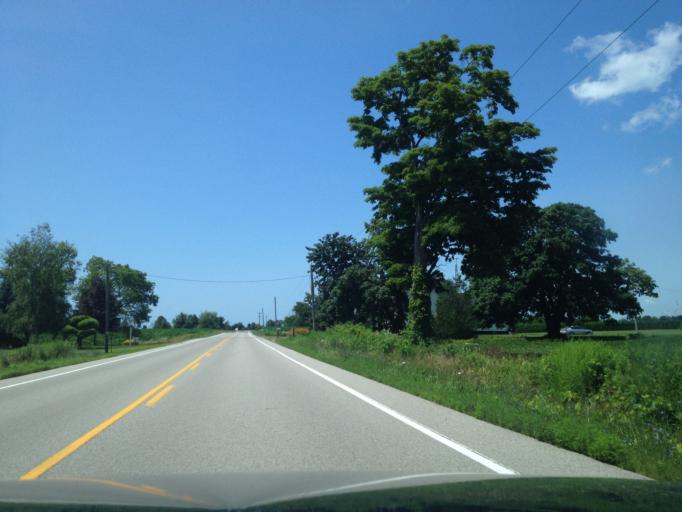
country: CA
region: Ontario
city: Norfolk County
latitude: 42.5769
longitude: -80.5362
